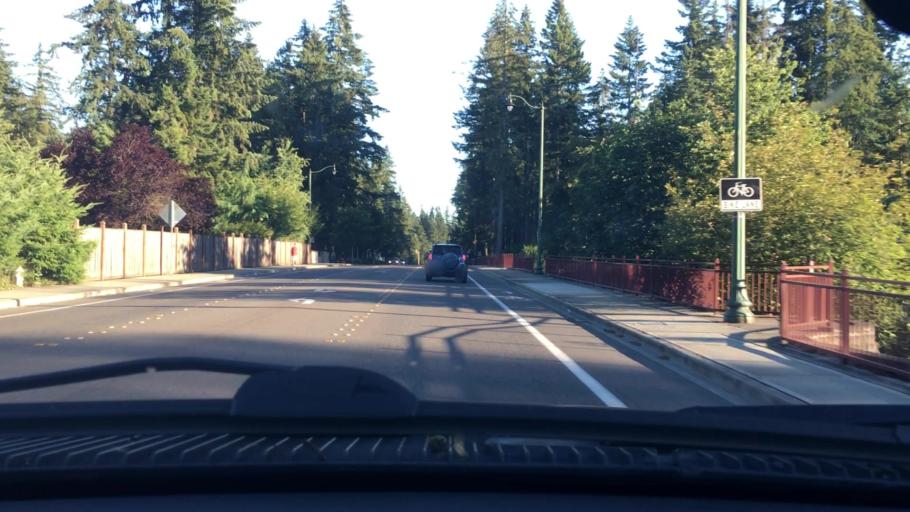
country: US
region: Washington
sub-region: King County
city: Maple Valley
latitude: 47.3829
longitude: -122.0482
